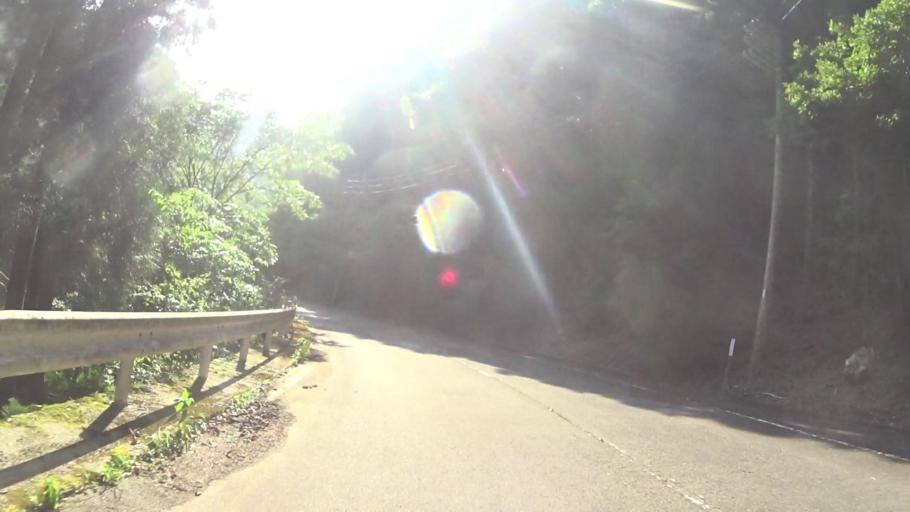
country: JP
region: Fukui
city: Obama
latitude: 35.2731
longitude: 135.6910
